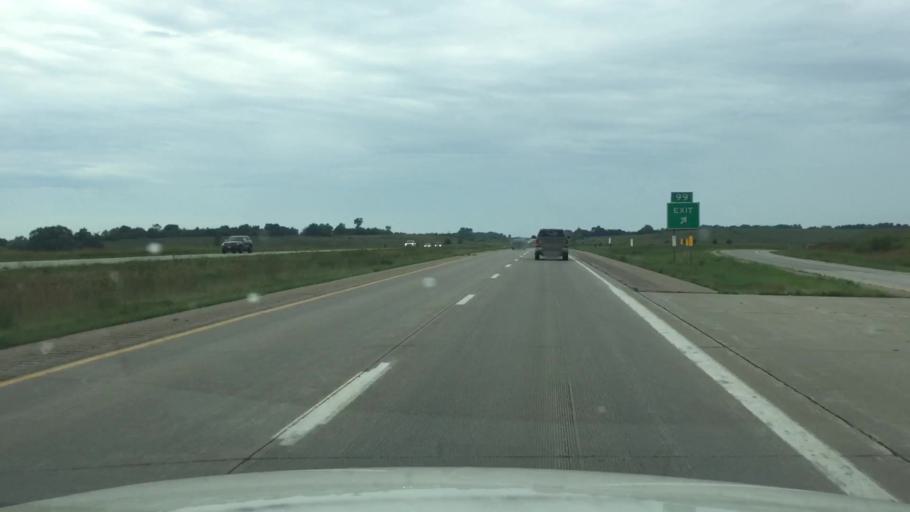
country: US
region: Iowa
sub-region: Warren County
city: Norwalk
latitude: 41.5143
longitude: -93.6747
